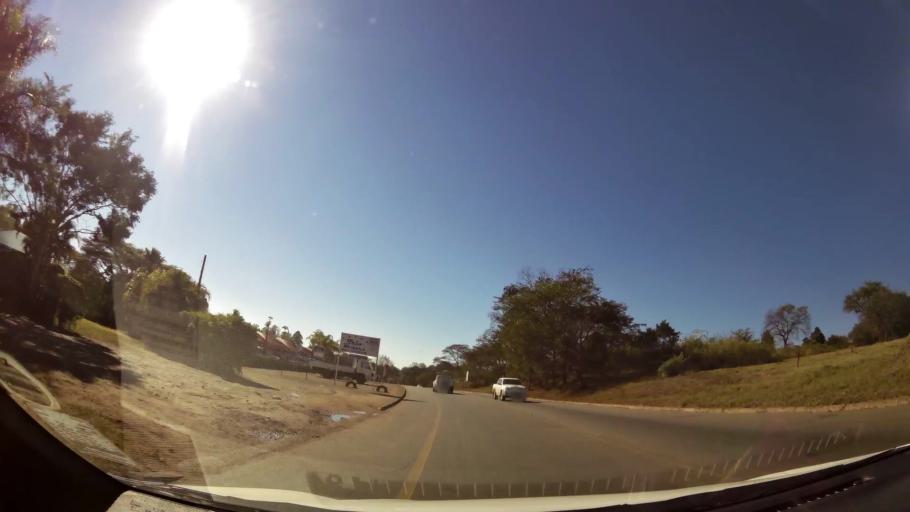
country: ZA
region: Limpopo
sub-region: Mopani District Municipality
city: Tzaneen
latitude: -23.8373
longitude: 30.1746
